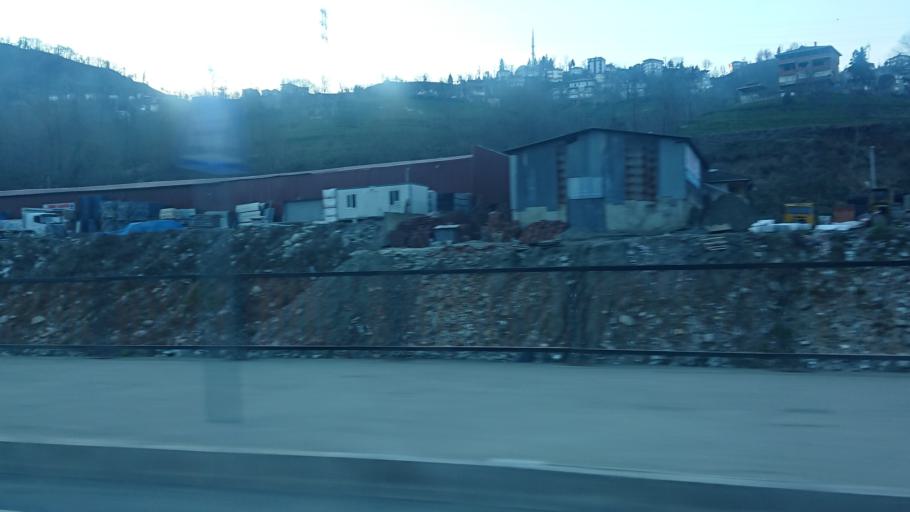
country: TR
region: Rize
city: Gundogdu
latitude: 41.0262
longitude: 40.5814
